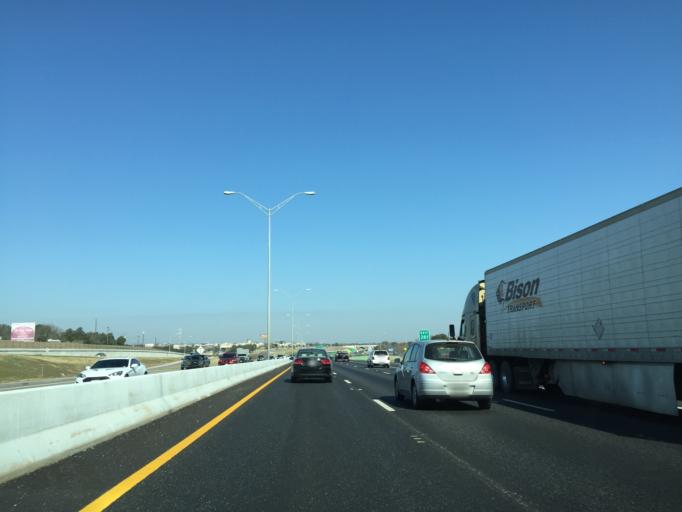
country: US
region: Texas
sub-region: Williamson County
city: Georgetown
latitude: 30.6218
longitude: -97.6899
